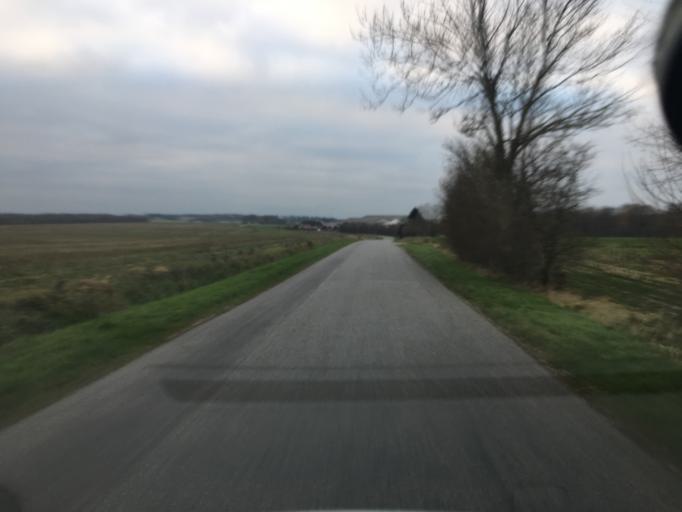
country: DK
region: South Denmark
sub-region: Tonder Kommune
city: Logumkloster
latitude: 55.0691
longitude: 9.0677
